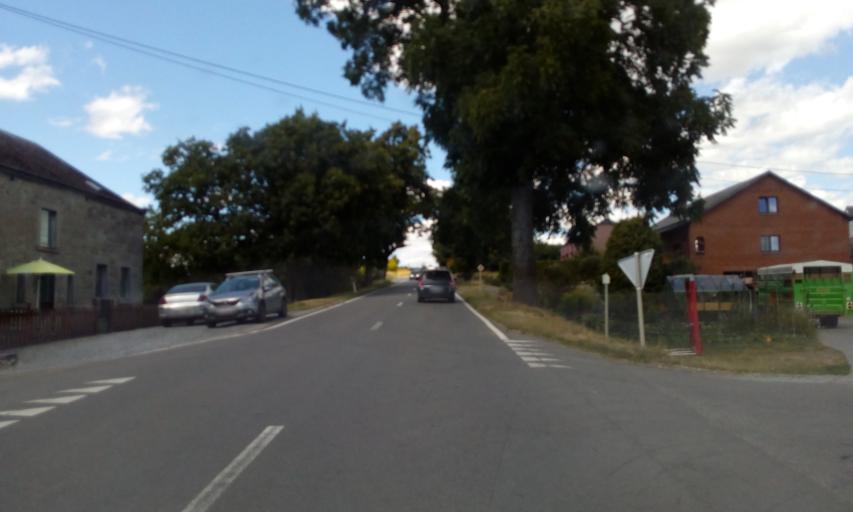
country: BE
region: Wallonia
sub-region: Province du Luxembourg
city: Wellin
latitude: 50.0790
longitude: 5.1328
